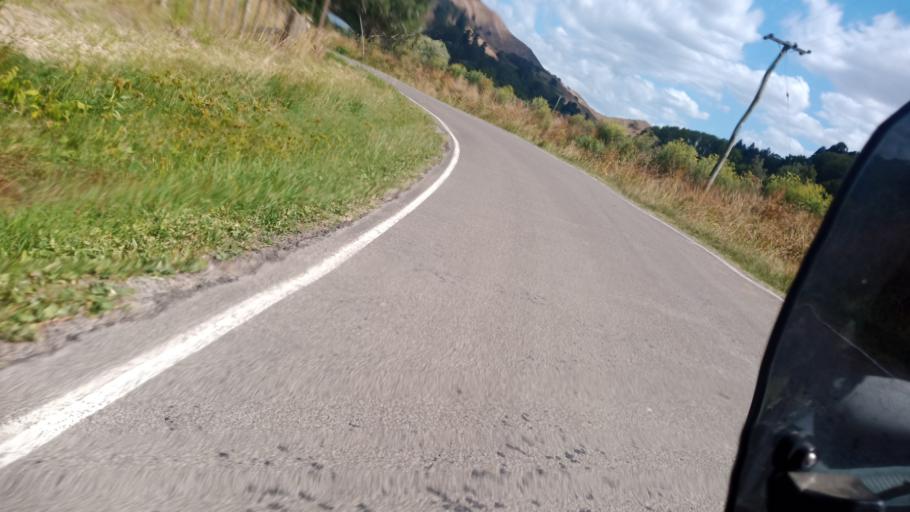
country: NZ
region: Gisborne
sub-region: Gisborne District
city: Gisborne
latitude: -38.6006
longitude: 177.7756
